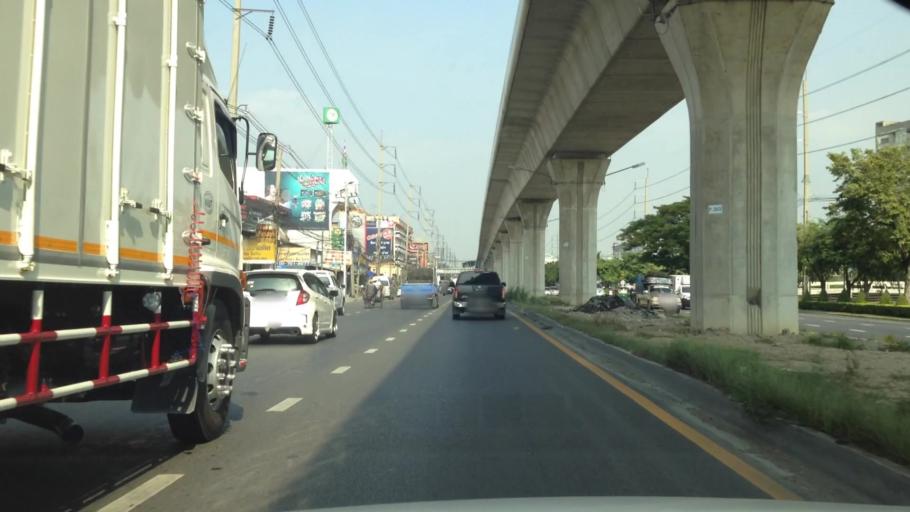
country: TH
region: Samut Prakan
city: Samut Prakan
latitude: 13.5615
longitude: 100.6106
